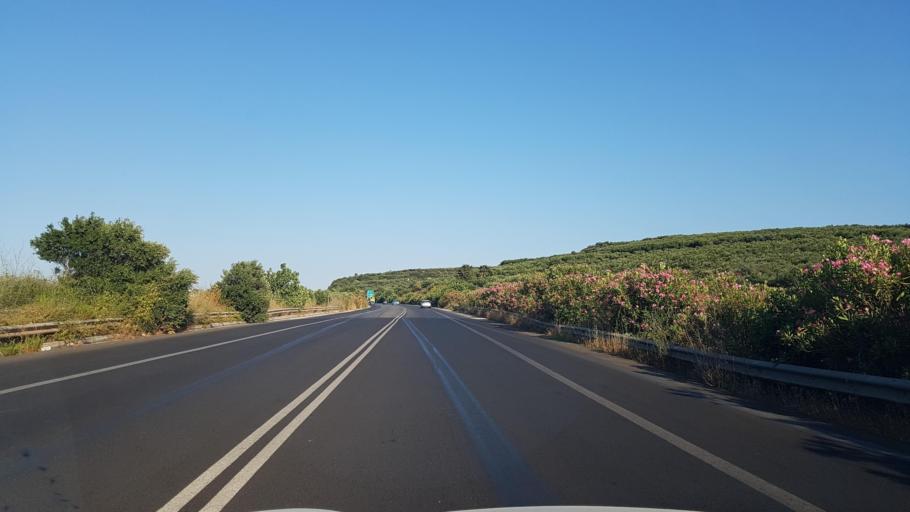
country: GR
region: Crete
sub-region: Nomos Chanias
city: Kolympari
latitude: 35.5256
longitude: 23.8011
